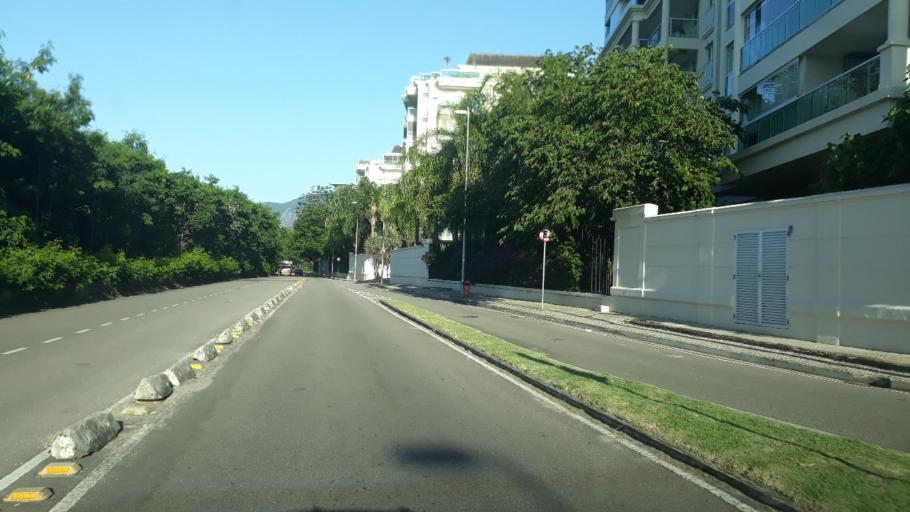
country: BR
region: Rio de Janeiro
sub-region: Rio De Janeiro
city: Rio de Janeiro
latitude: -22.9969
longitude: -43.3493
